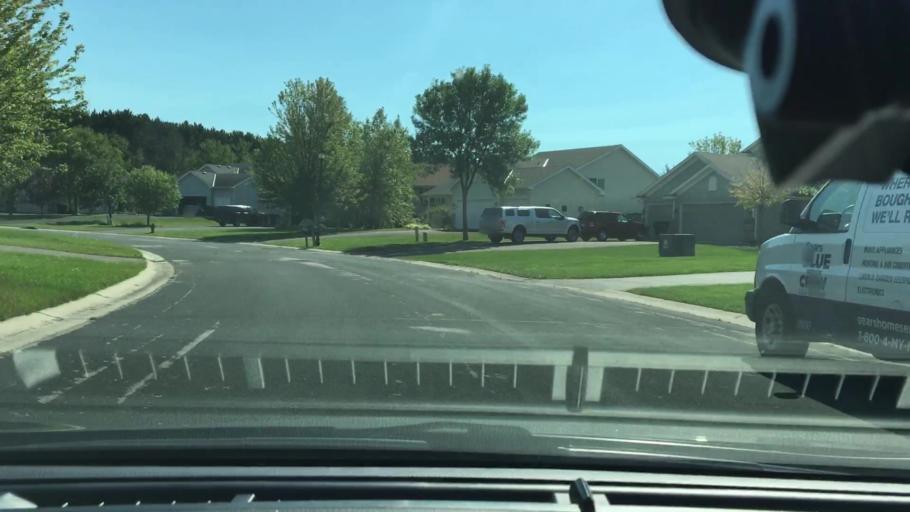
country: US
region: Minnesota
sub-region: Wright County
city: Hanover
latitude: 45.1631
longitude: -93.6775
